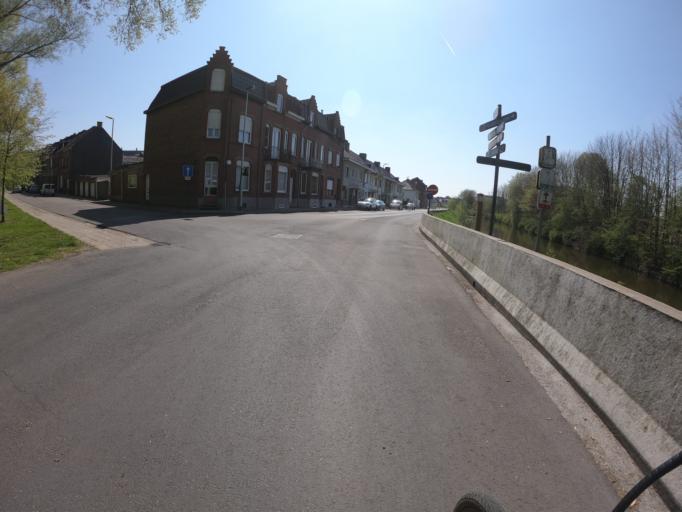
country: BE
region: Flanders
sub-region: Provincie Oost-Vlaanderen
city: Geraardsbergen
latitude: 50.7771
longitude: 3.8801
